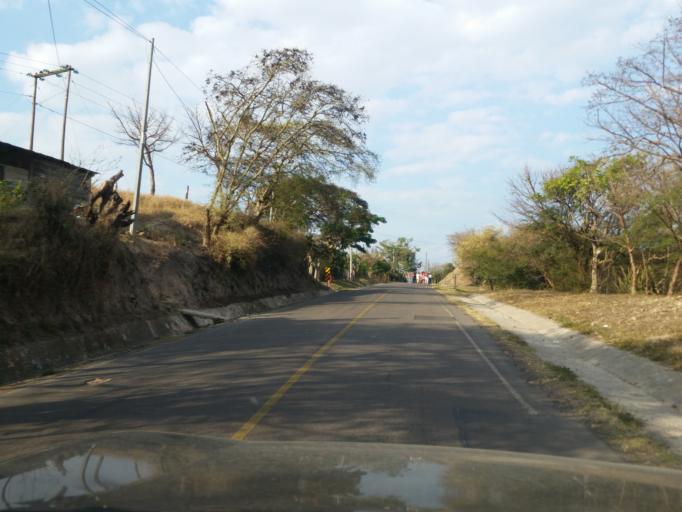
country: NI
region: Jinotega
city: San Rafael del Norte
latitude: 13.1956
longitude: -86.1190
